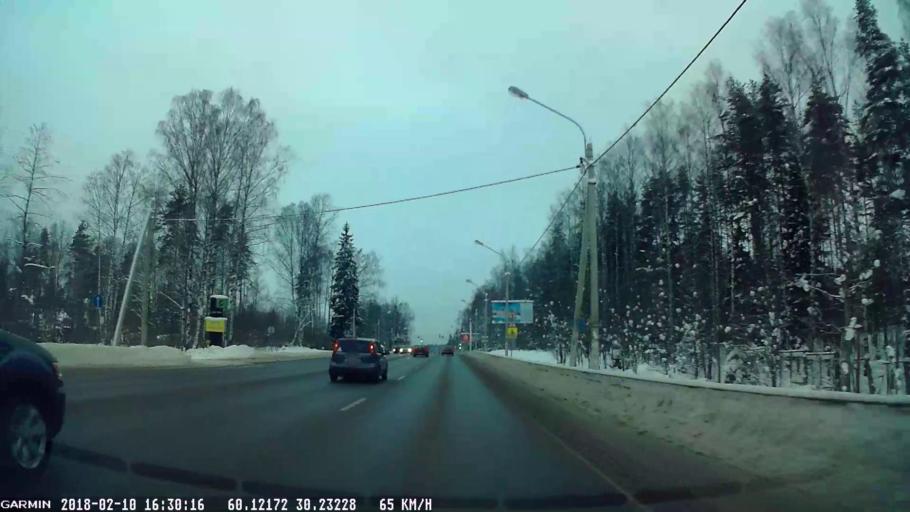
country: RU
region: St.-Petersburg
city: Levashovo
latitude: 60.1223
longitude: 30.2317
